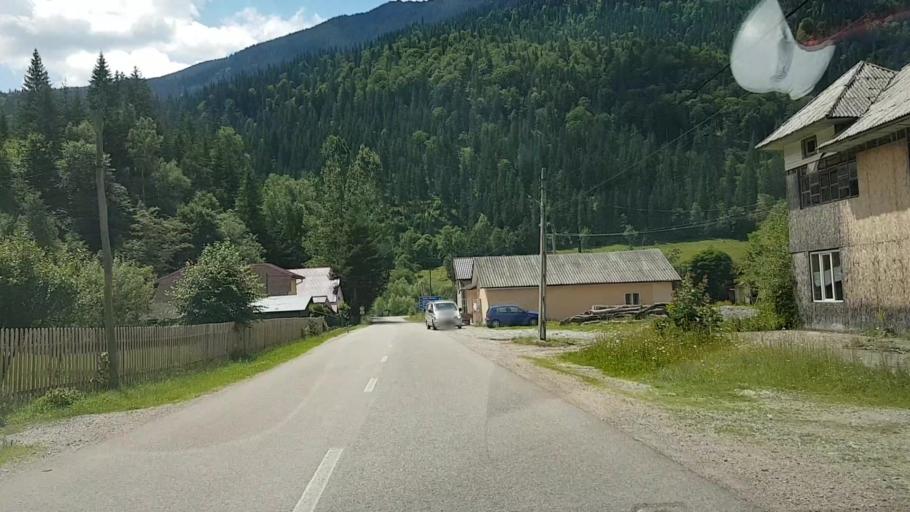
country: RO
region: Suceava
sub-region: Comuna Crucea
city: Crucea
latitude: 47.3977
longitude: 25.5651
